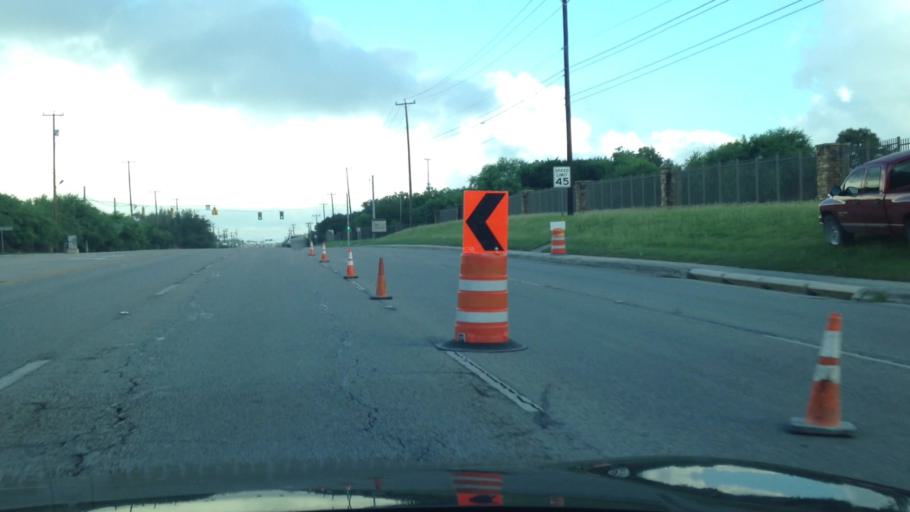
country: US
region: Texas
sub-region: Bexar County
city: Shavano Park
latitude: 29.5388
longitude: -98.5790
